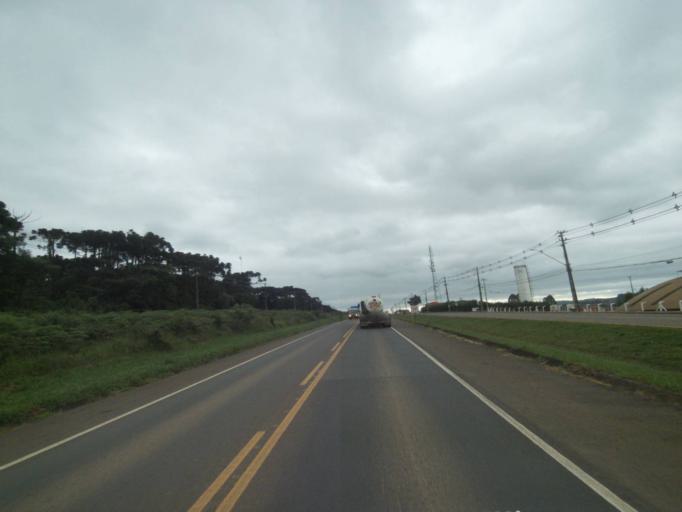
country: BR
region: Parana
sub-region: Telemaco Borba
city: Telemaco Borba
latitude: -24.3748
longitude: -50.6650
